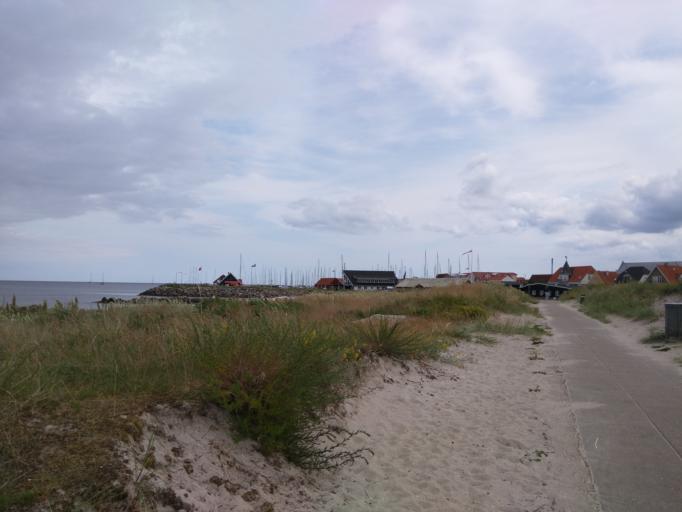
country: DK
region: North Denmark
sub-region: Frederikshavn Kommune
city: Saeby
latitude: 57.3358
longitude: 10.5275
